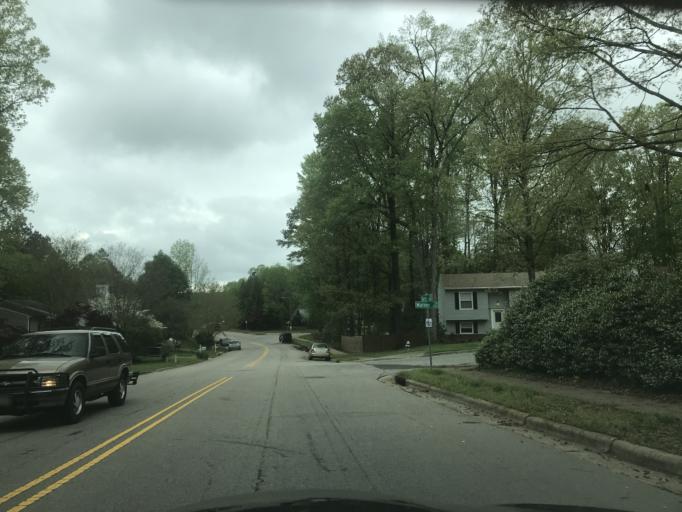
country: US
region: North Carolina
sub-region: Wake County
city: West Raleigh
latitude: 35.7520
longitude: -78.6777
